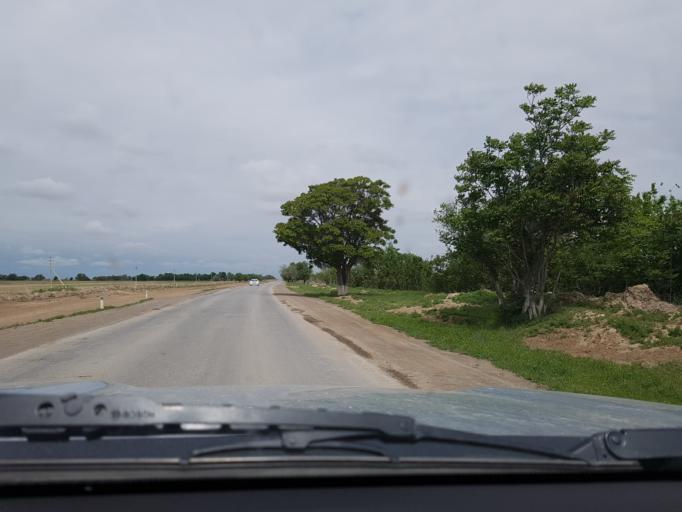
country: TM
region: Mary
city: Bayramaly
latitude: 37.7323
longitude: 62.0981
